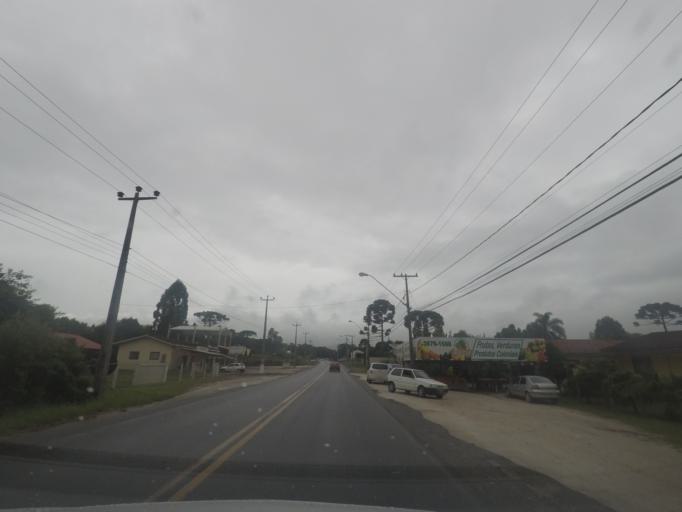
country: BR
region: Parana
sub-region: Campina Grande Do Sul
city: Campina Grande do Sul
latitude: -25.3179
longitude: -49.0753
